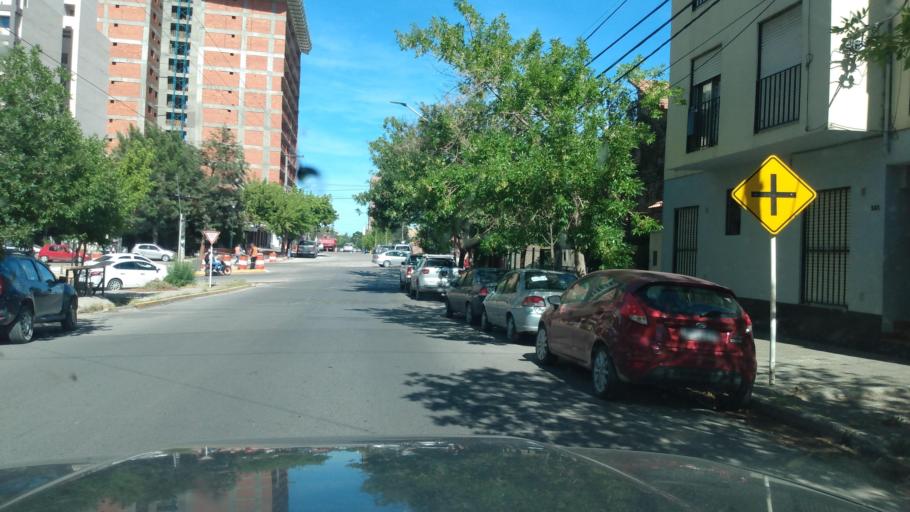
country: AR
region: Neuquen
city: Neuquen
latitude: -38.9475
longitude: -68.0627
